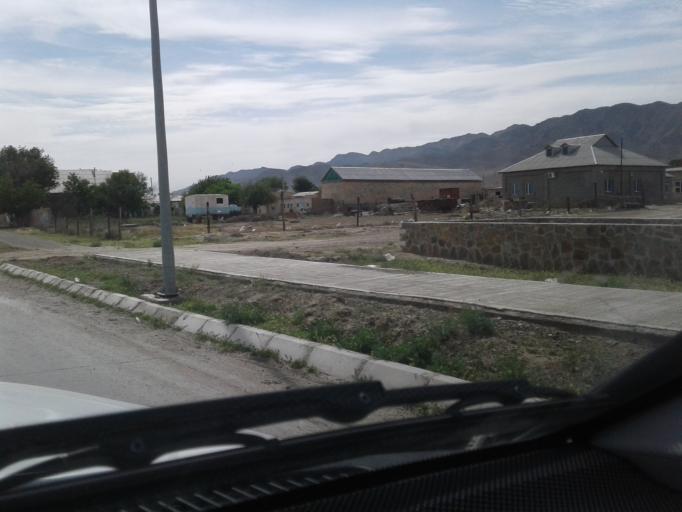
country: TM
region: Balkan
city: Gazanjyk
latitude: 39.2454
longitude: 55.4995
